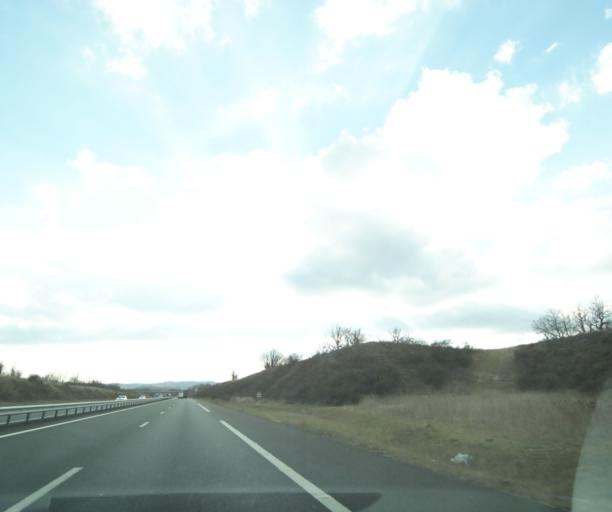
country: FR
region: Midi-Pyrenees
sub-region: Departement du Lot
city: Pradines
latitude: 44.5788
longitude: 1.5140
